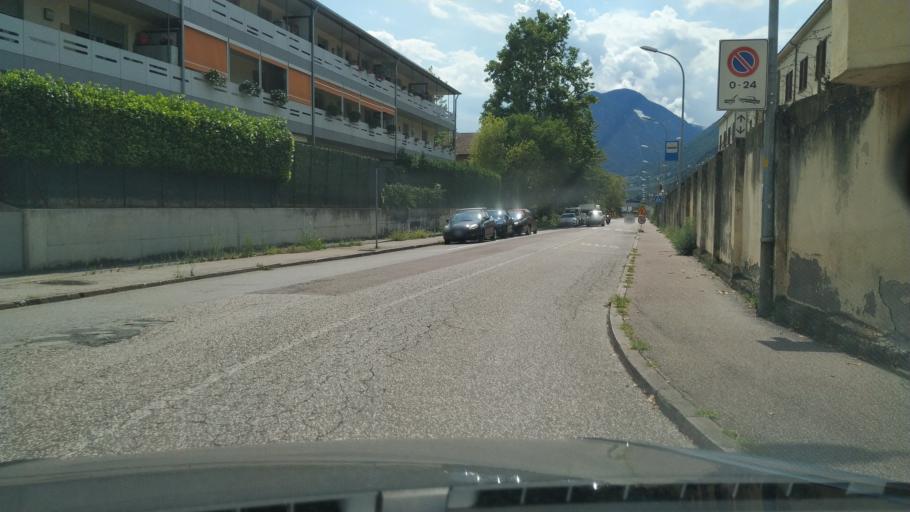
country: IT
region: Trentino-Alto Adige
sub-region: Bolzano
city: Merano
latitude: 46.6599
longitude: 11.1604
